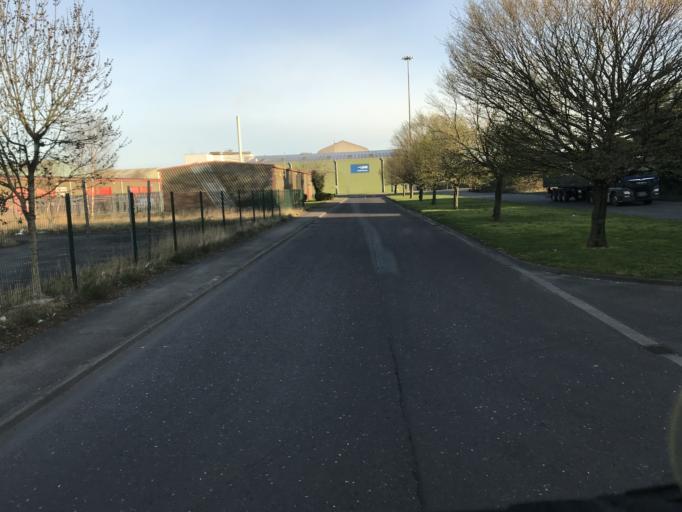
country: GB
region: England
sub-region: North Lincolnshire
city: Burton upon Stather
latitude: 53.6196
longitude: -0.6978
